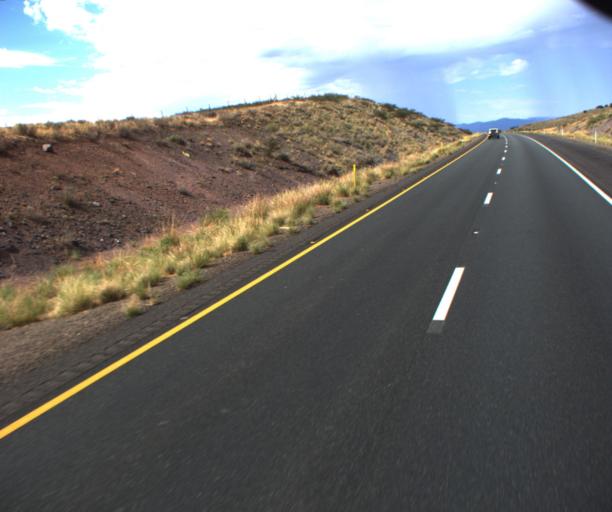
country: US
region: Arizona
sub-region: Yavapai County
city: Cordes Lakes
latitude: 34.4407
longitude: -112.0412
